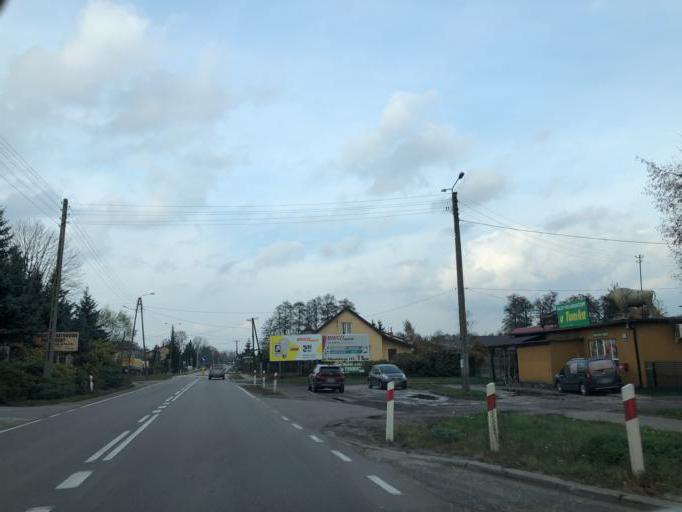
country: PL
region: Podlasie
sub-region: Lomza
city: Lomza
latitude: 53.1326
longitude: 22.0410
